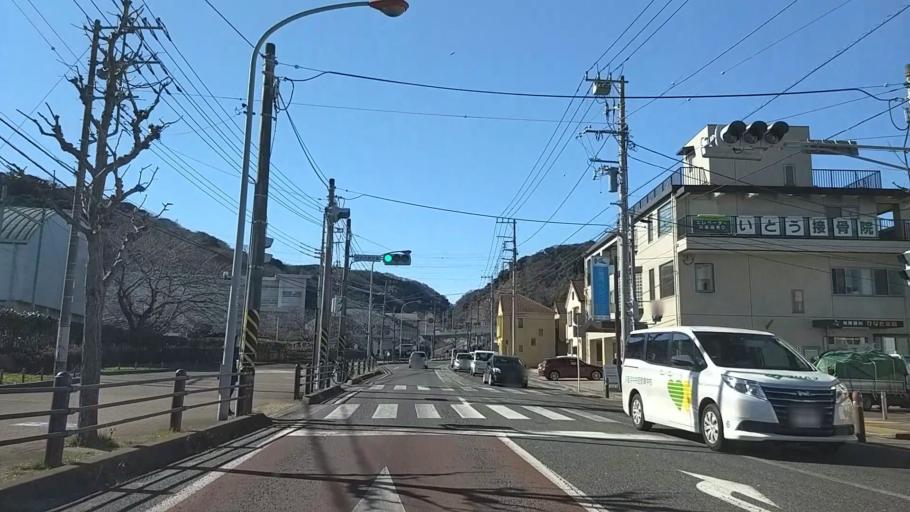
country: JP
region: Kanagawa
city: Yokosuka
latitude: 35.2269
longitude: 139.7012
